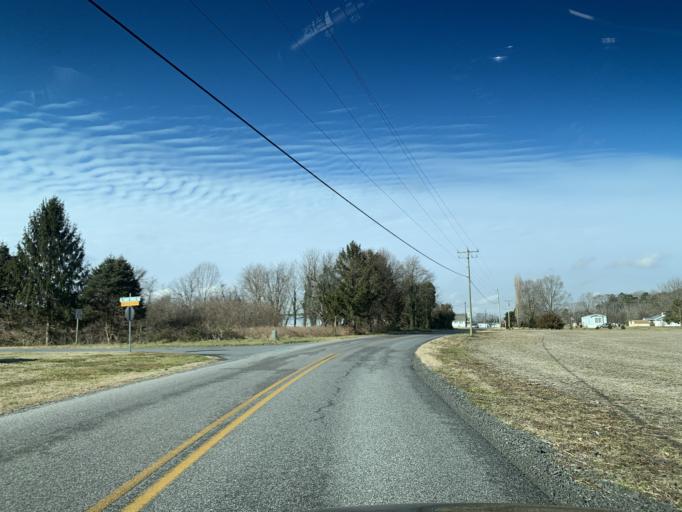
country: US
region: Maryland
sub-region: Worcester County
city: Ocean Pines
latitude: 38.4261
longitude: -75.1719
